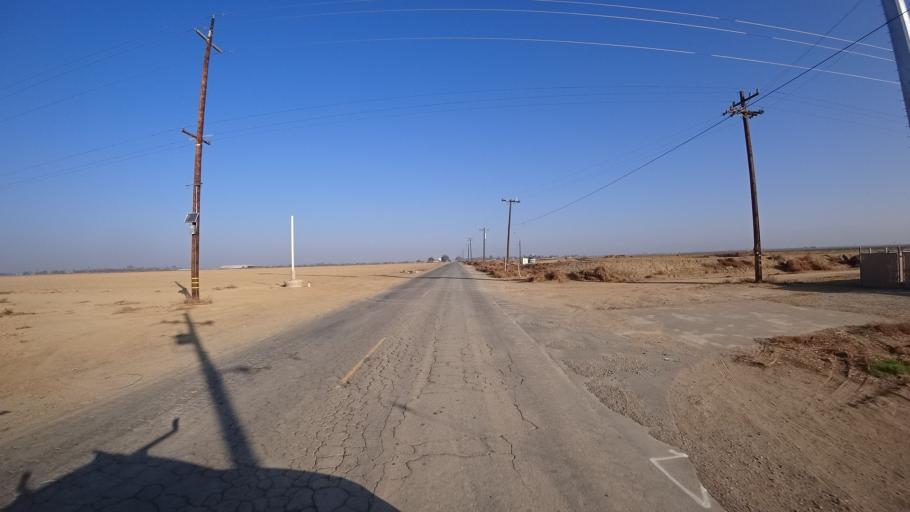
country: US
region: California
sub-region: Kern County
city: Weedpatch
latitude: 35.2228
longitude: -118.9677
